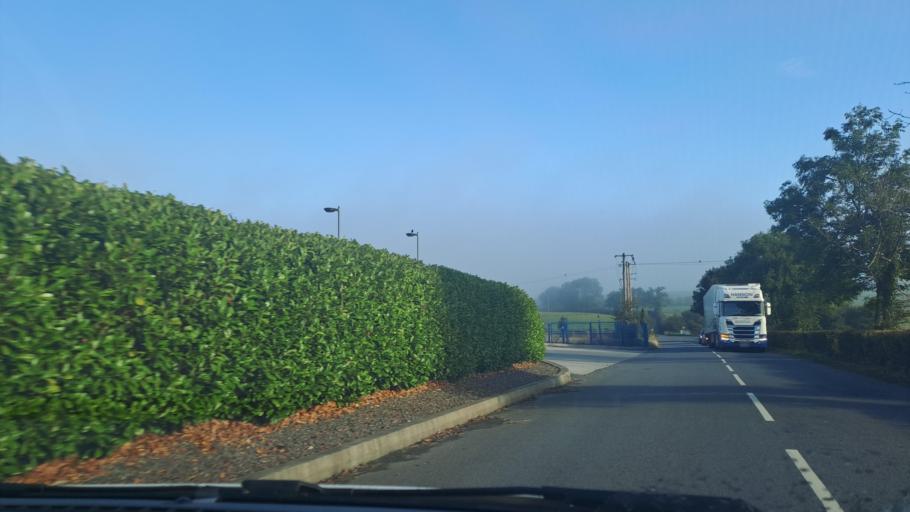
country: IE
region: Ulster
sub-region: An Cabhan
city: Kingscourt
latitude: 53.9952
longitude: -6.8542
